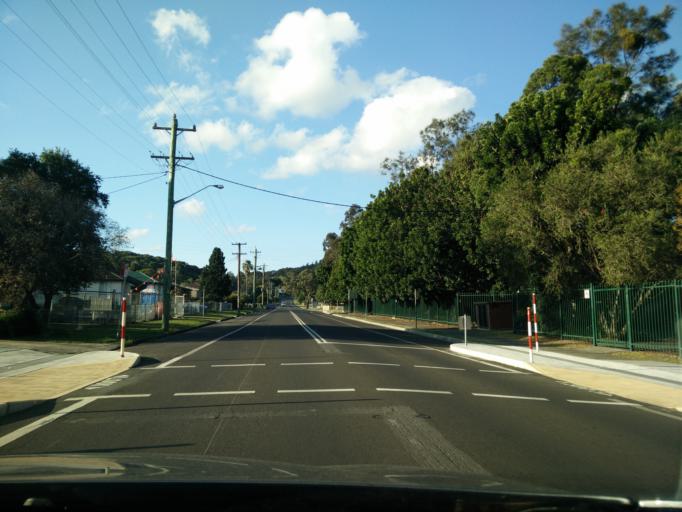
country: AU
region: New South Wales
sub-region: Wollongong
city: Berkeley
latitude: -34.4754
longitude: 150.8401
